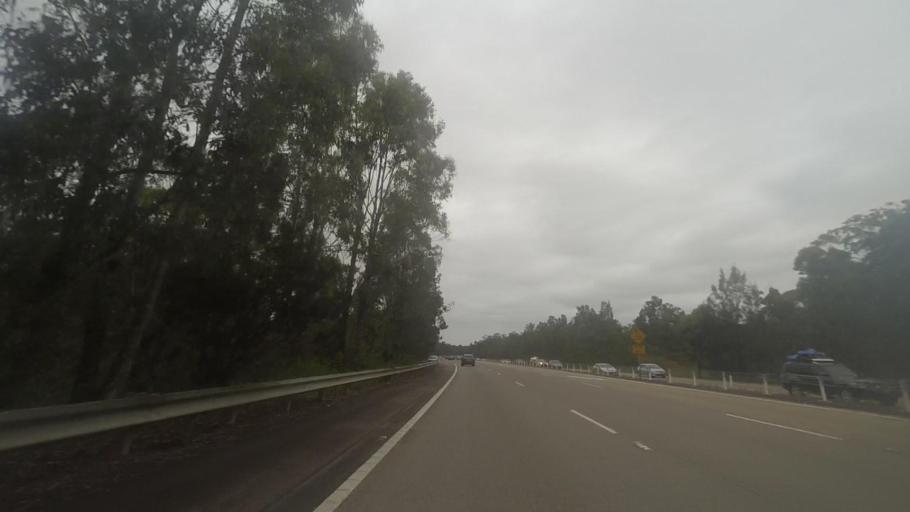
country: AU
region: New South Wales
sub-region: Port Stephens Shire
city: Medowie
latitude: -32.6883
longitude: 151.8095
